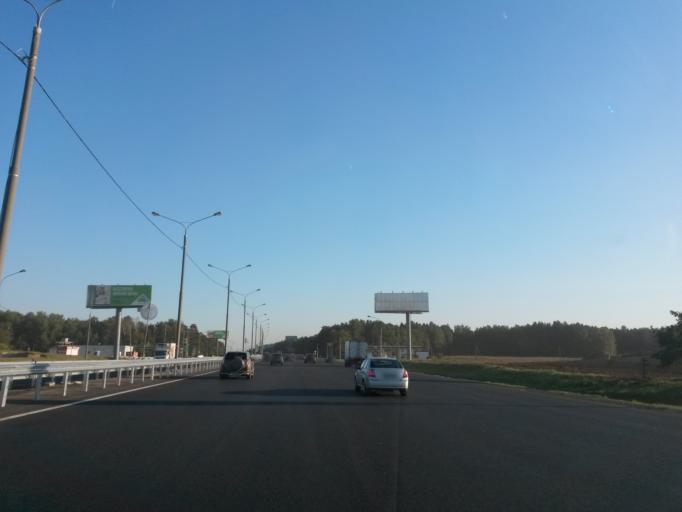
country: RU
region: Moskovskaya
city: Shcherbinka
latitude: 55.5228
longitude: 37.6091
